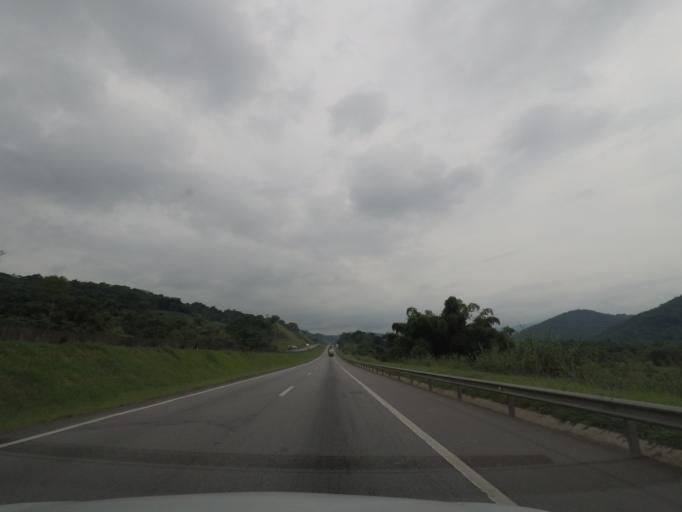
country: BR
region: Sao Paulo
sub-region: Miracatu
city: Miracatu
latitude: -24.1703
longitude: -47.3392
